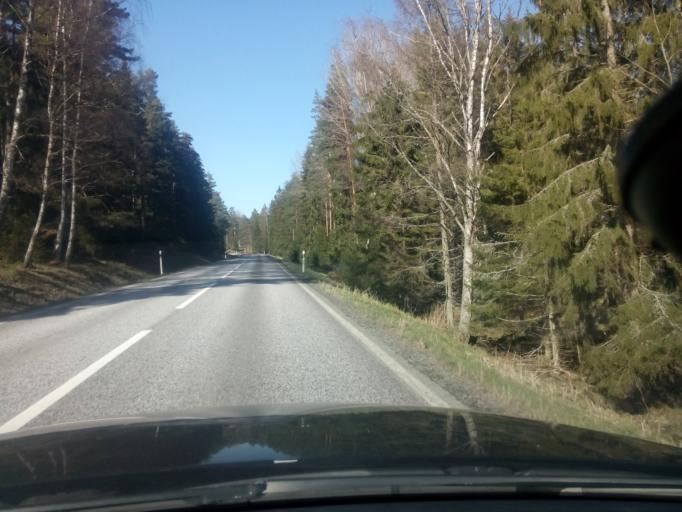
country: SE
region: Soedermanland
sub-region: Nykopings Kommun
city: Stigtomta
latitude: 58.9337
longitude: 16.8448
